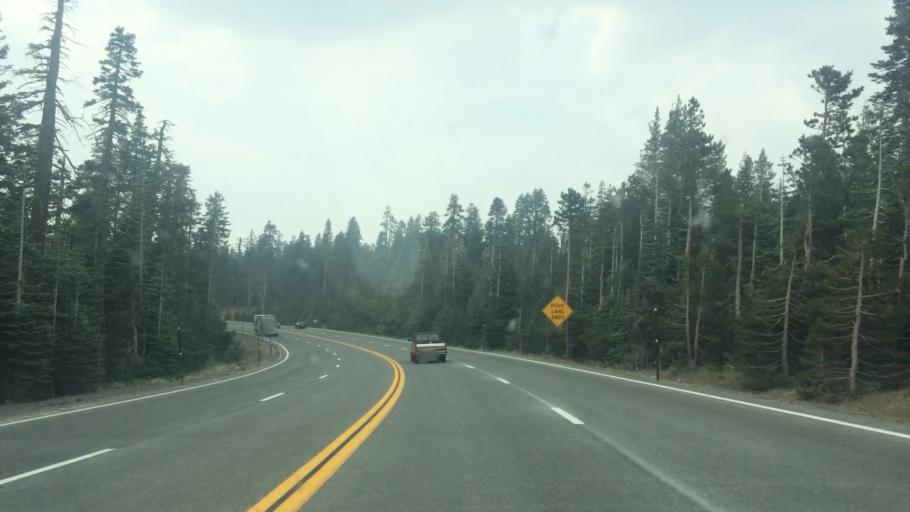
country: US
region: California
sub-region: El Dorado County
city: South Lake Tahoe
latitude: 38.6308
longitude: -120.1913
